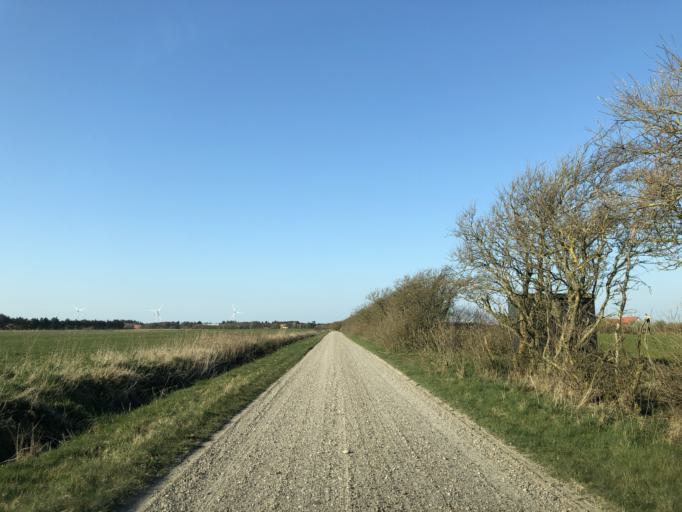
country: DK
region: Central Jutland
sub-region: Holstebro Kommune
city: Ulfborg
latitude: 56.3544
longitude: 8.2483
